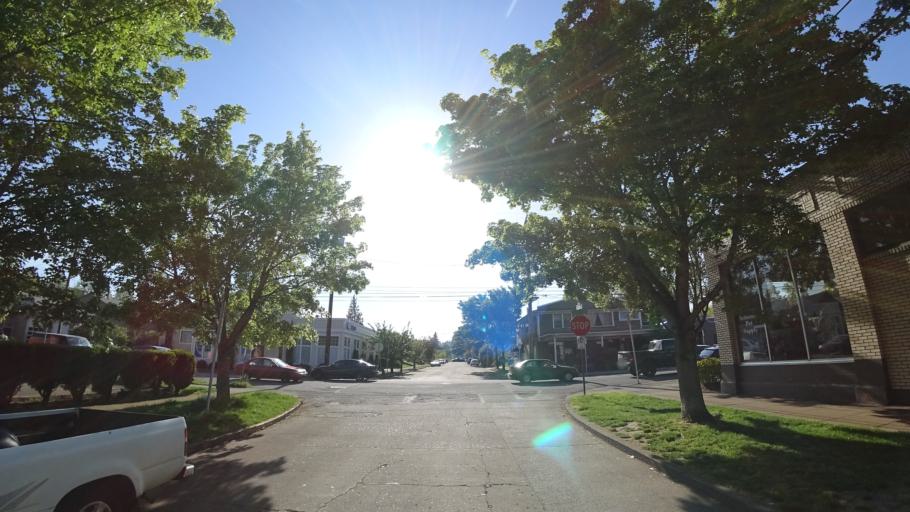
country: US
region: Oregon
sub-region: Clackamas County
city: Milwaukie
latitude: 45.4621
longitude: -122.6468
